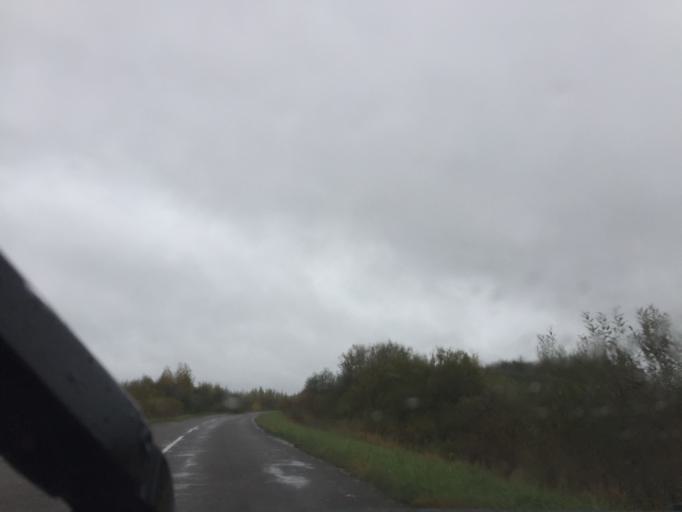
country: LV
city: Tireli
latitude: 56.8114
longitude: 23.5765
